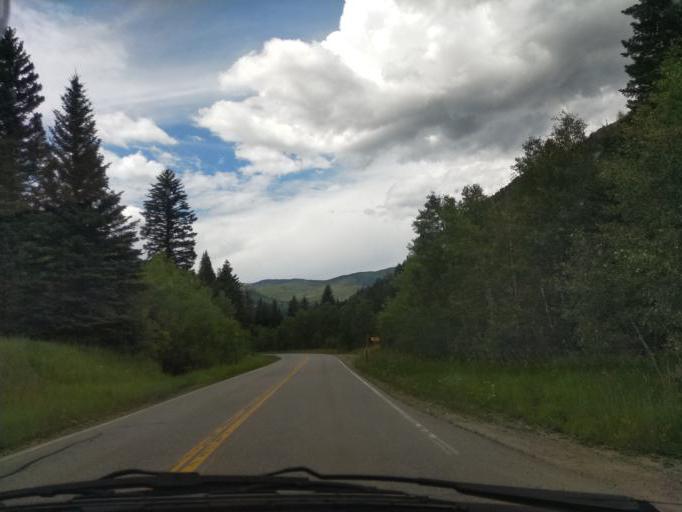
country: US
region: Colorado
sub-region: Garfield County
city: Carbondale
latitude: 39.0979
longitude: -107.2582
